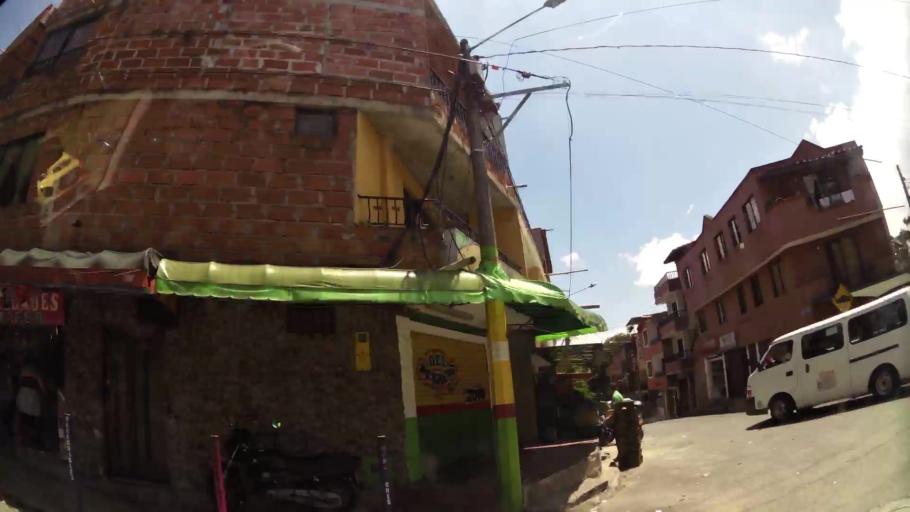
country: CO
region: Antioquia
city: La Estrella
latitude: 6.1831
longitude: -75.6434
